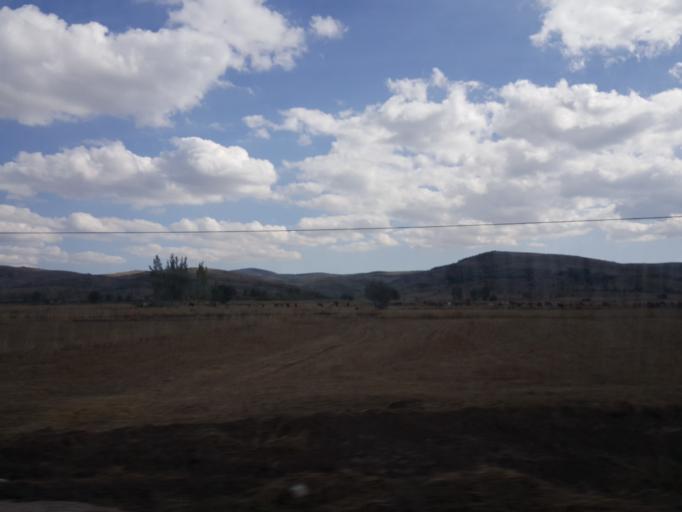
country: TR
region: Tokat
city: Yesilyurt
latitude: 40.0237
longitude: 36.2820
